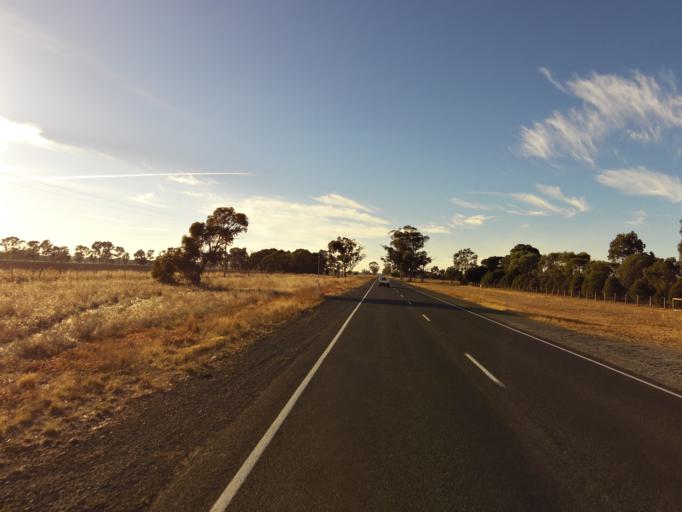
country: AU
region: New South Wales
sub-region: Murray Shire
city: Moama
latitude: -36.1002
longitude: 144.6839
